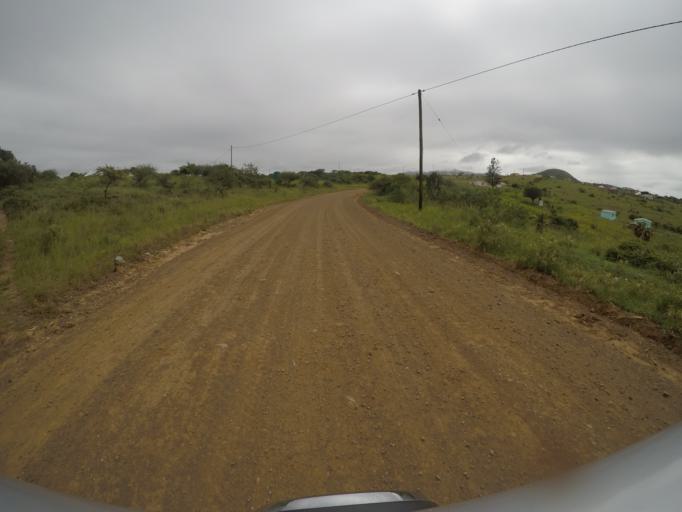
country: ZA
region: KwaZulu-Natal
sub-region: uThungulu District Municipality
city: Empangeni
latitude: -28.6039
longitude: 31.8384
